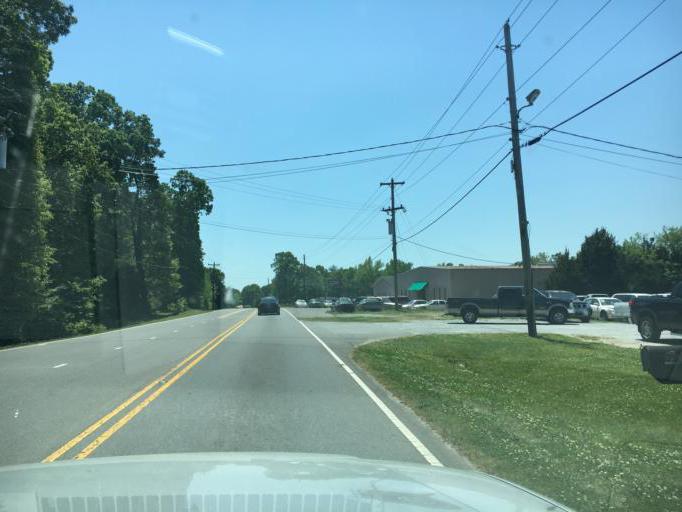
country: US
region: North Carolina
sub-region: Cleveland County
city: Shelby
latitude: 35.2565
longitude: -81.5645
